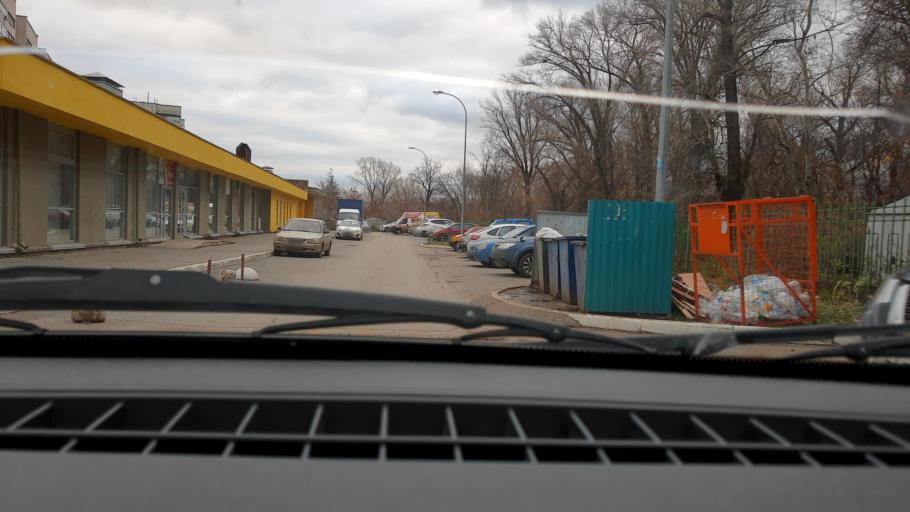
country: RU
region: Bashkortostan
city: Ufa
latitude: 54.7754
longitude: 56.1082
